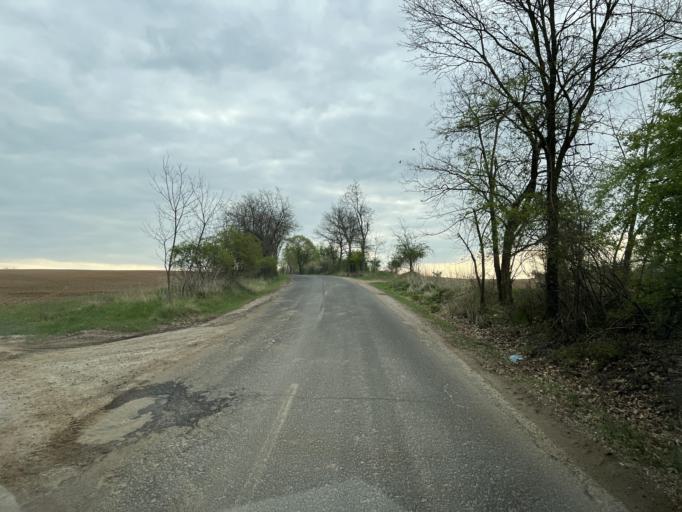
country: HU
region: Pest
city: Acsa
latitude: 47.7897
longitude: 19.4064
